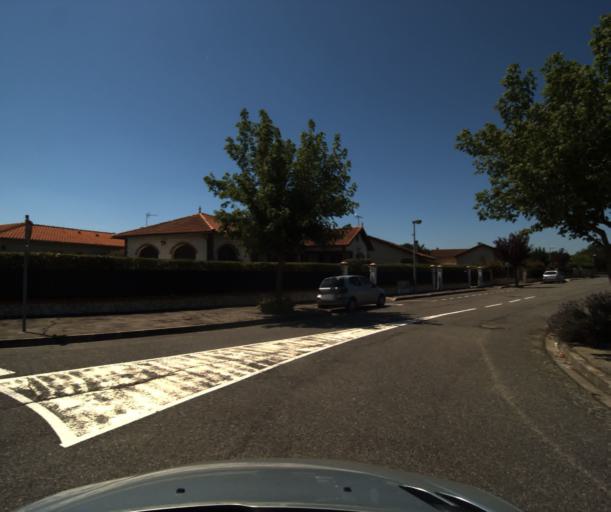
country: FR
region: Midi-Pyrenees
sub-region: Departement de la Haute-Garonne
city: Roquettes
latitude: 43.4953
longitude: 1.3652
